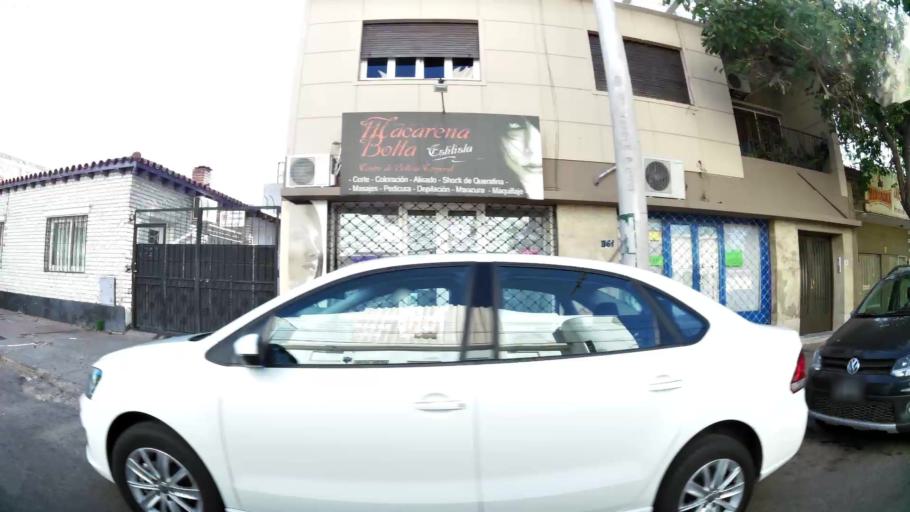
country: AR
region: Mendoza
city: Mendoza
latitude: -32.9004
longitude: -68.8288
